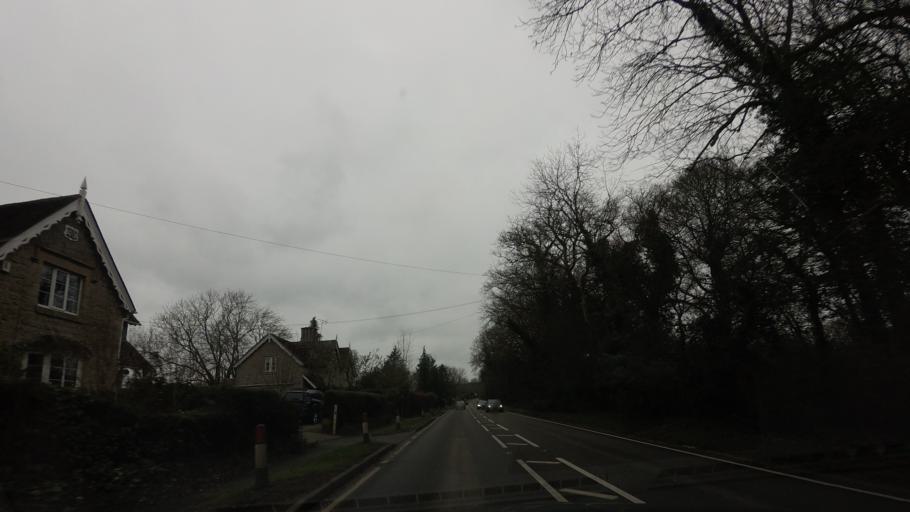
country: GB
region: England
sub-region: Kent
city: Marden
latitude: 51.2158
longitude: 0.5123
